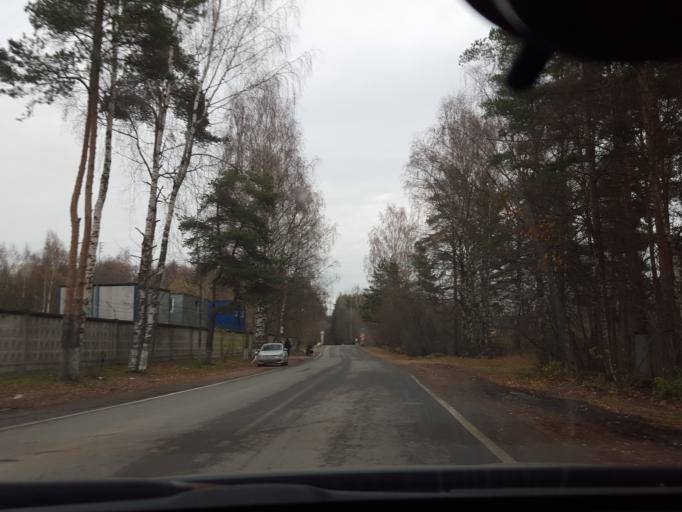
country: RU
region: St.-Petersburg
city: Shuvalovo
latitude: 60.0462
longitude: 30.2681
